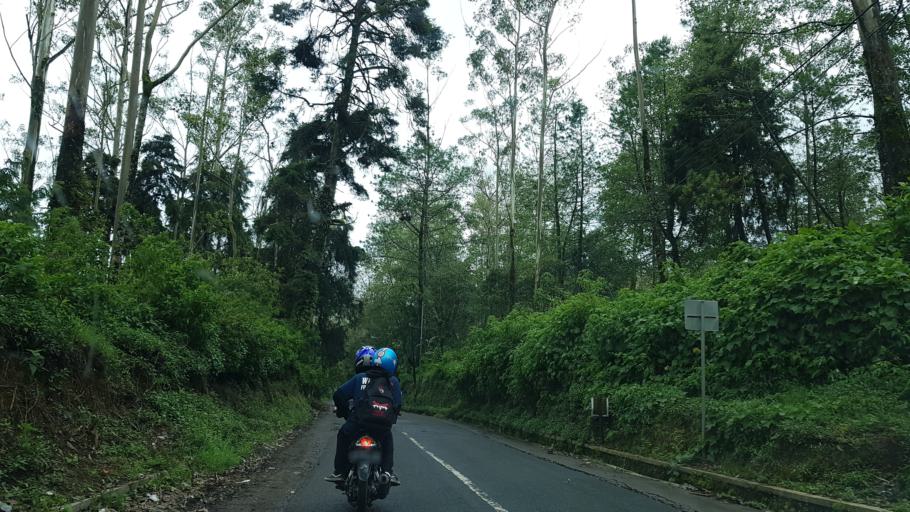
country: ID
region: West Java
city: Banjar
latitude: -7.1406
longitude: 107.3983
